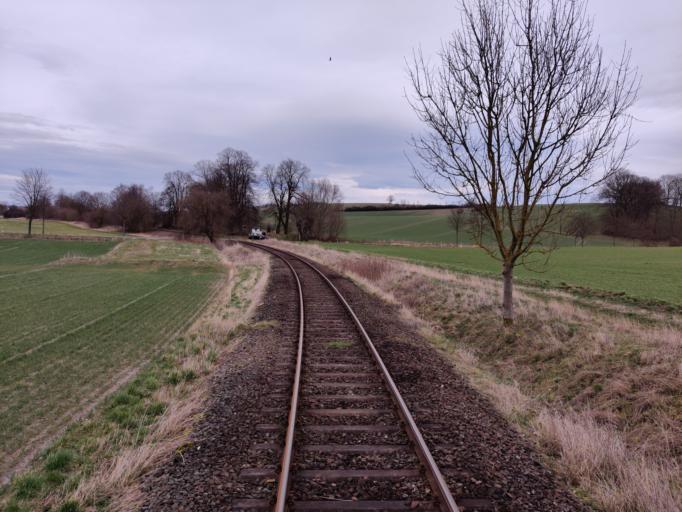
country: DE
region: Lower Saxony
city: Haverlah
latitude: 52.0694
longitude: 10.1475
